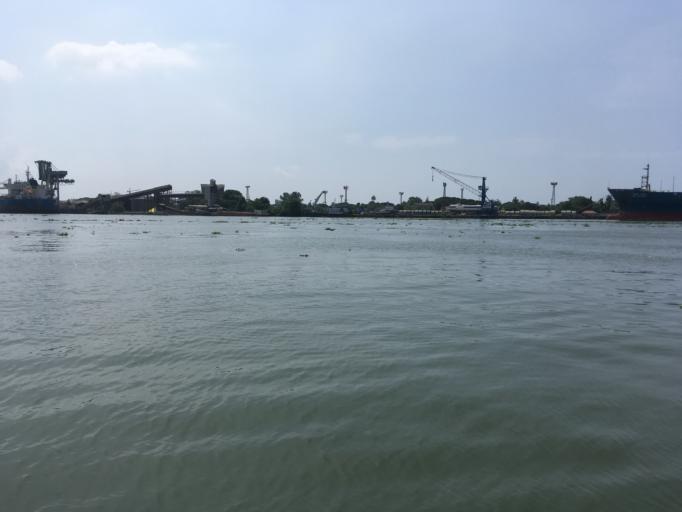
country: IN
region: Kerala
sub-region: Ernakulam
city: Cochin
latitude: 9.9699
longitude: 76.2715
